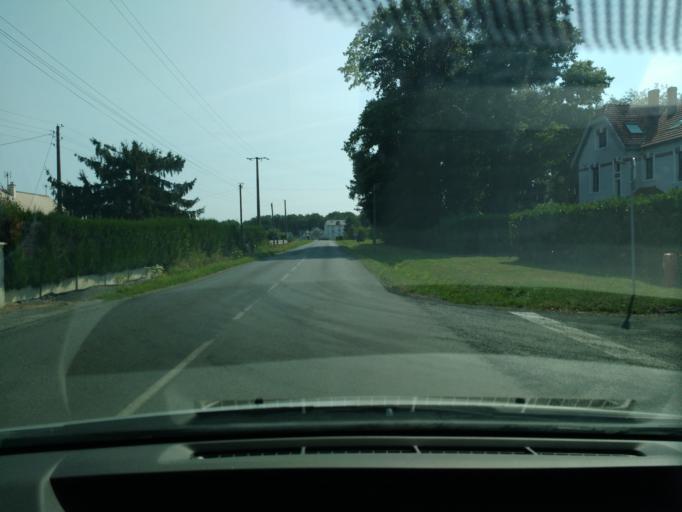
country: FR
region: Pays de la Loire
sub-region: Departement de Maine-et-Loire
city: Baune
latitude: 47.4828
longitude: -0.3103
